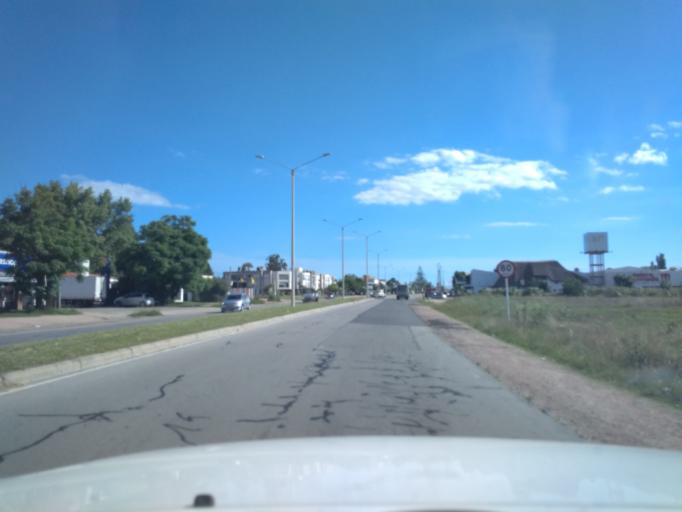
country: UY
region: Canelones
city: Barra de Carrasco
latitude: -34.8679
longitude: -56.0213
